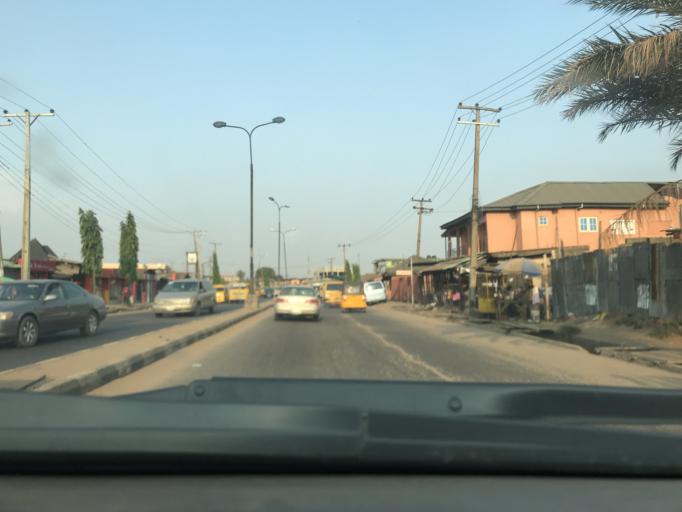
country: NG
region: Lagos
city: Agege
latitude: 6.6106
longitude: 3.2948
